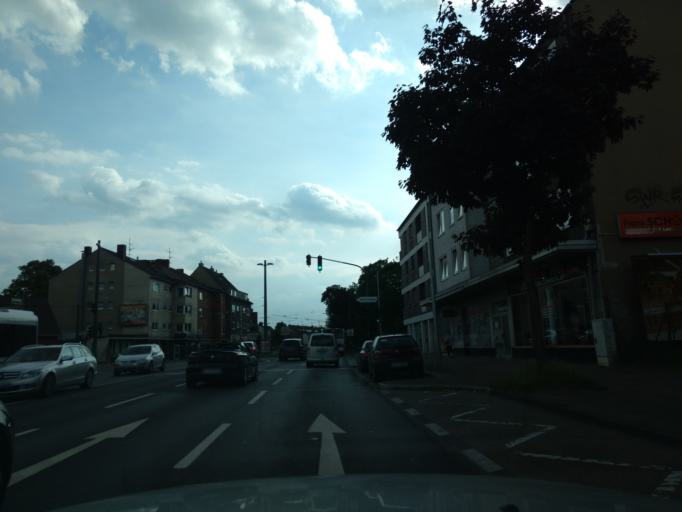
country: DE
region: North Rhine-Westphalia
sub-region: Regierungsbezirk Dusseldorf
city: Dusseldorf
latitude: 51.2753
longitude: 6.7842
